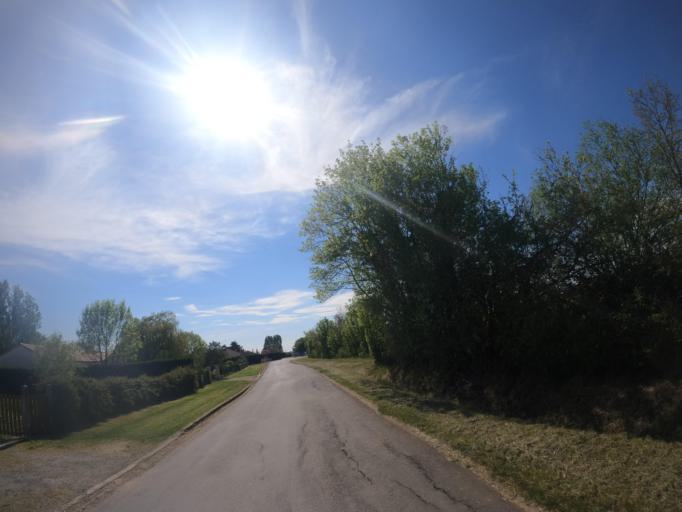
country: FR
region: Poitou-Charentes
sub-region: Departement des Deux-Sevres
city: Airvault
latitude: 46.8830
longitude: -0.1579
